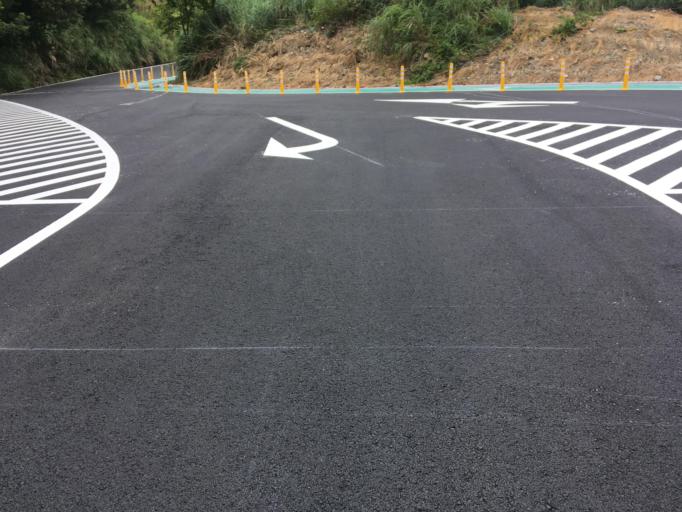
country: TW
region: Taiwan
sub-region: Yilan
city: Yilan
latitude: 24.4999
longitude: 121.5326
